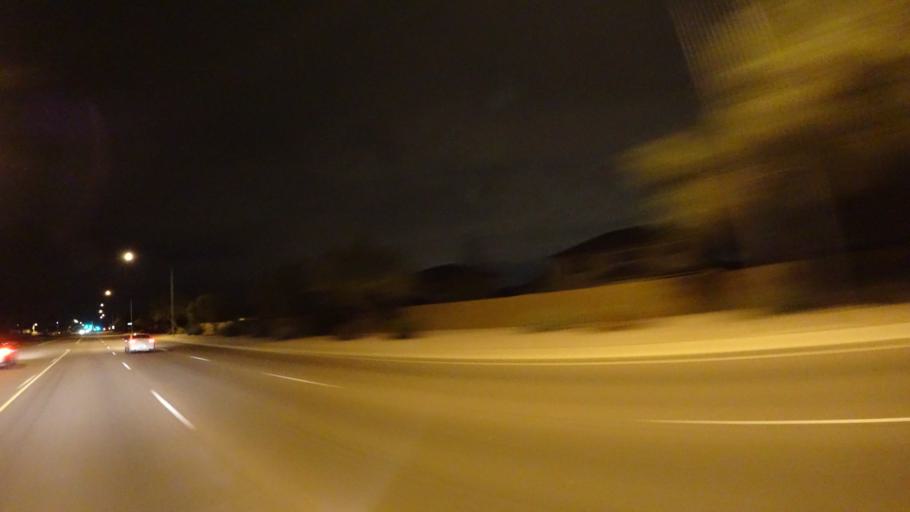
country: US
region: Arizona
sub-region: Pinal County
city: Apache Junction
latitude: 33.4121
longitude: -111.5981
